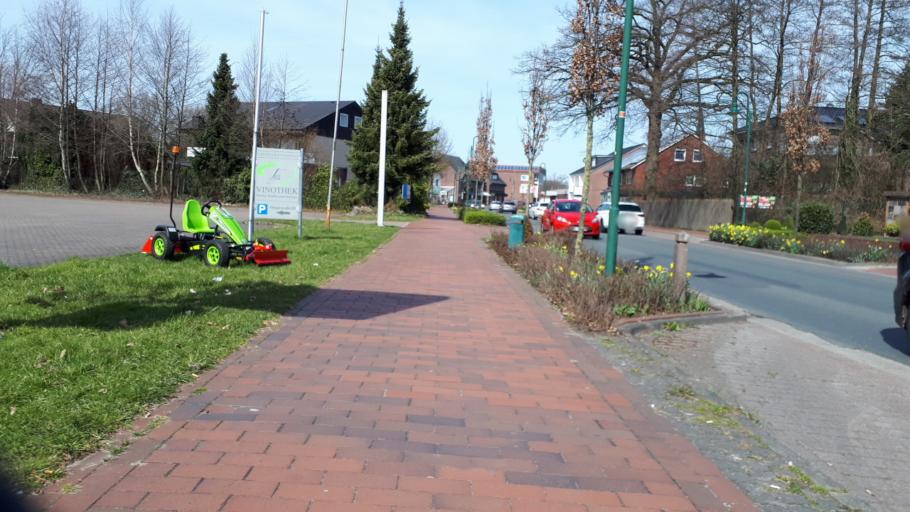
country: DE
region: Lower Saxony
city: Garrel
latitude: 52.9530
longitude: 8.0258
